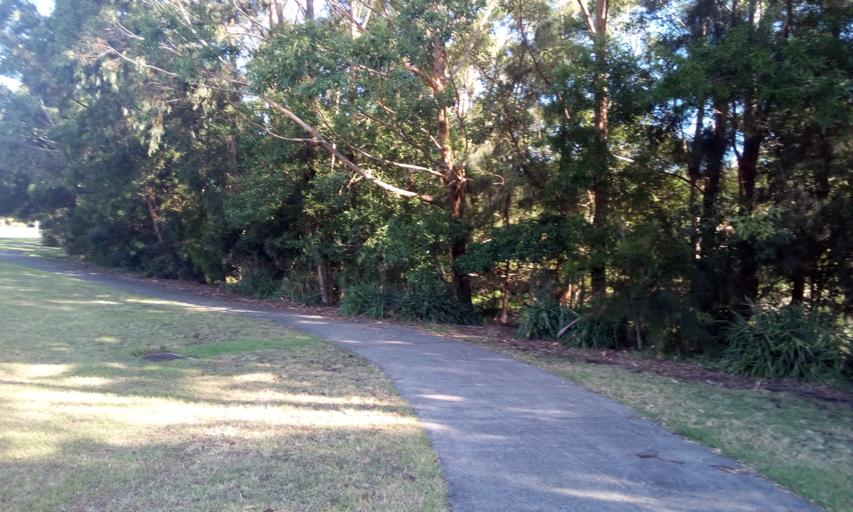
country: AU
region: New South Wales
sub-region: Wollongong
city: West Wollongong
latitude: -34.4253
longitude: 150.8607
